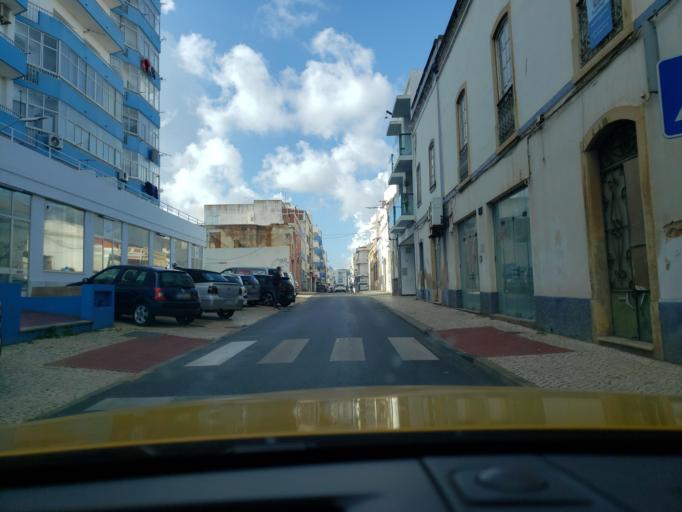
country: PT
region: Faro
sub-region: Portimao
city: Portimao
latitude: 37.1410
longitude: -8.5340
